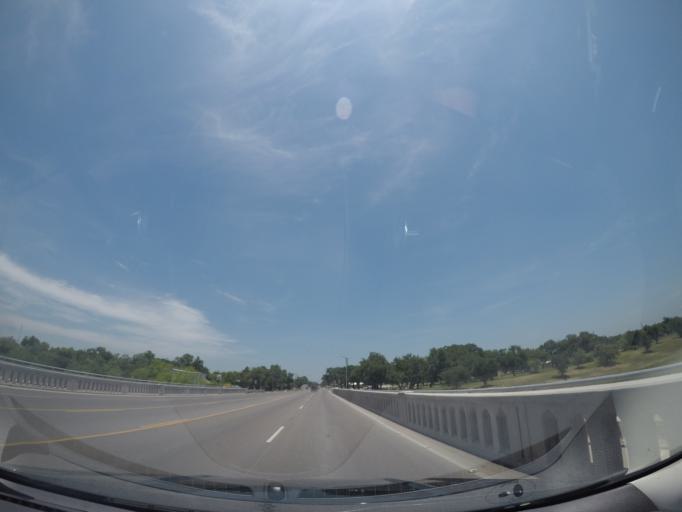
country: US
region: Texas
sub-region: Uvalde County
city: Uvalde
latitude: 29.2036
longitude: -99.8017
